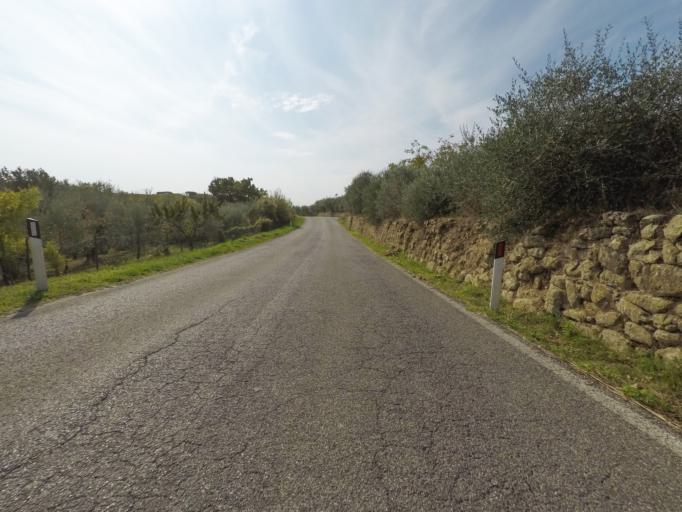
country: IT
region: Tuscany
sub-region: Provincia di Siena
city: Belverde
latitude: 43.4033
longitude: 11.3526
